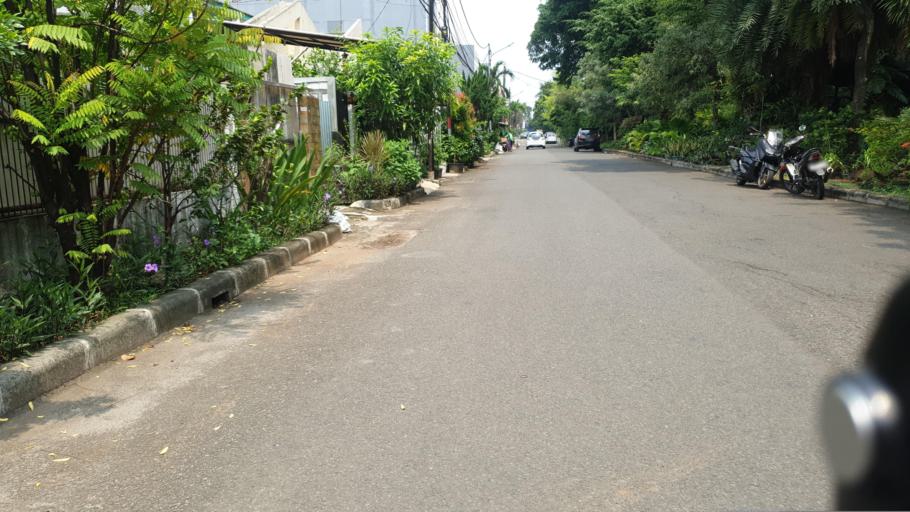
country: ID
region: West Java
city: Ciputat
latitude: -6.1940
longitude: 106.7458
